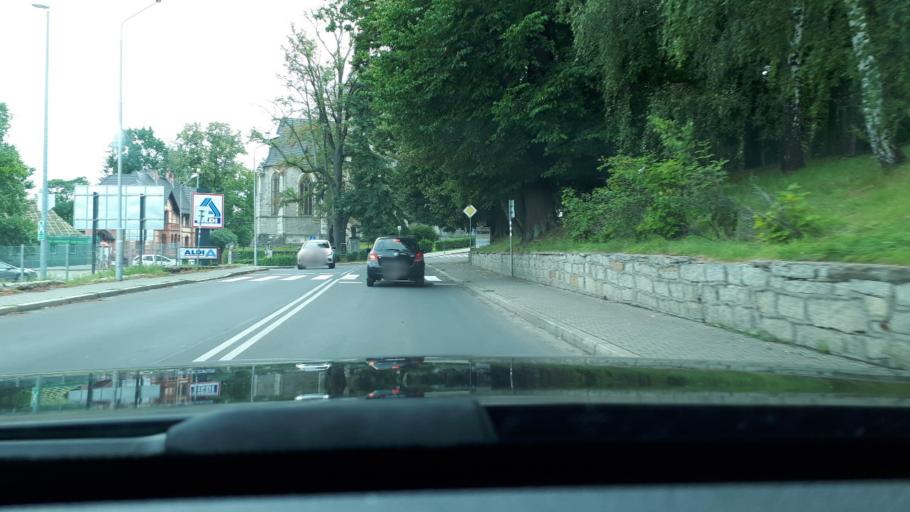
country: PL
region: Lower Silesian Voivodeship
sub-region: Powiat lubanski
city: Luban
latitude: 51.1161
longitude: 15.2893
